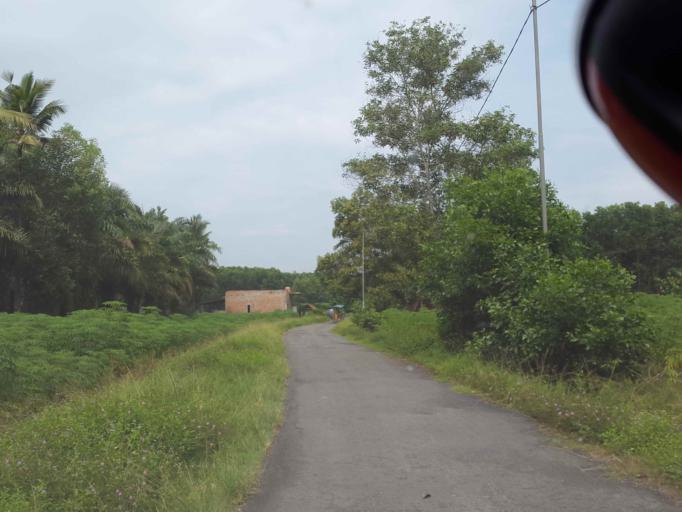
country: ID
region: Lampung
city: Natar
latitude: -5.2544
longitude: 105.2058
